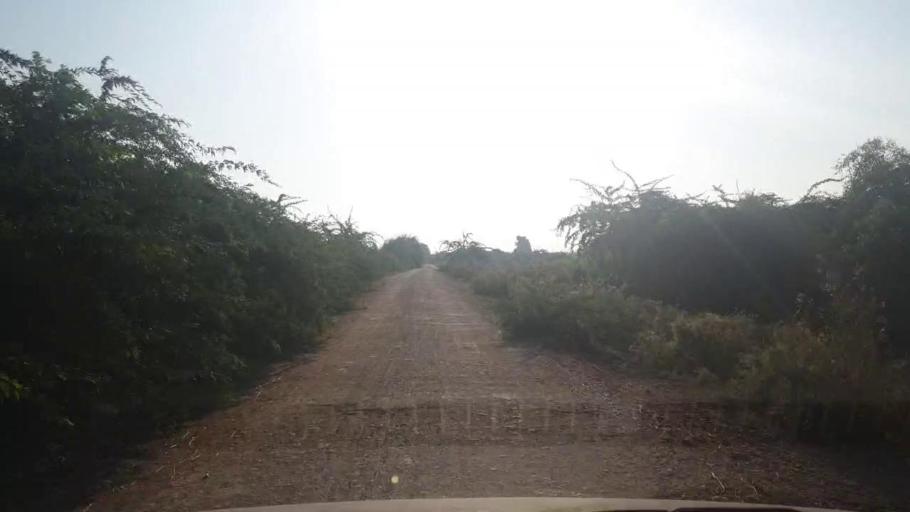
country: PK
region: Sindh
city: Badin
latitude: 24.7349
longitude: 68.8739
